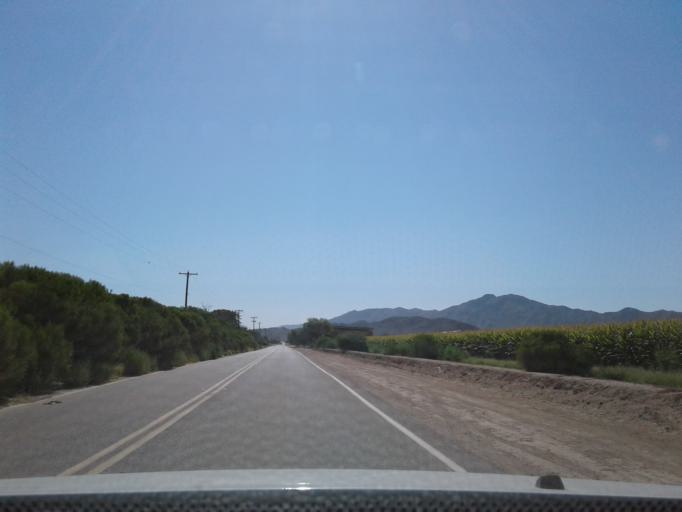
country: US
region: Arizona
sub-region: Maricopa County
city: Laveen
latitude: 33.3487
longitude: -112.1822
